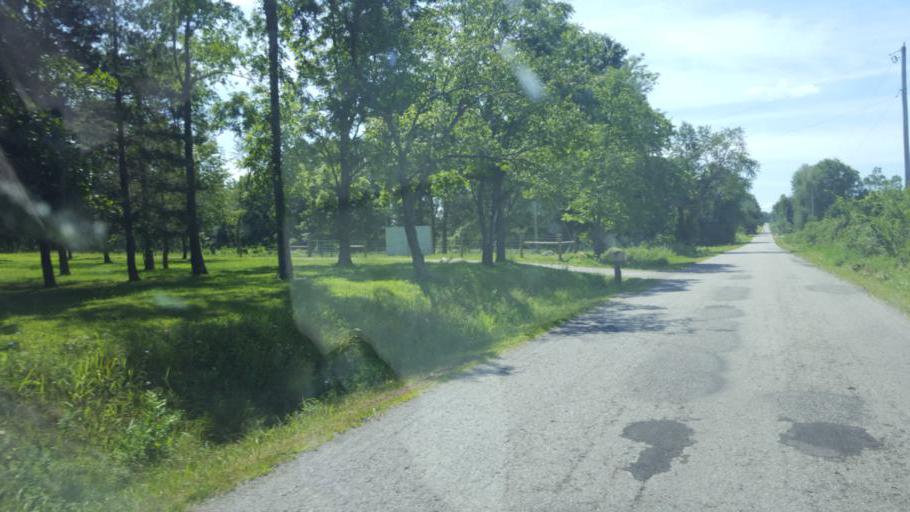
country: US
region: Ohio
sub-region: Knox County
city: Centerburg
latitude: 40.4198
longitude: -82.7388
